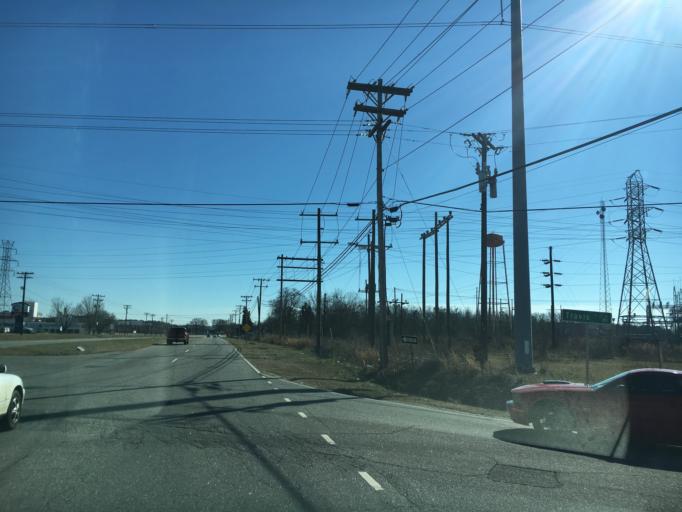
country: US
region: South Carolina
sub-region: Anderson County
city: Homeland Park
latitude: 34.4405
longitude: -82.6651
